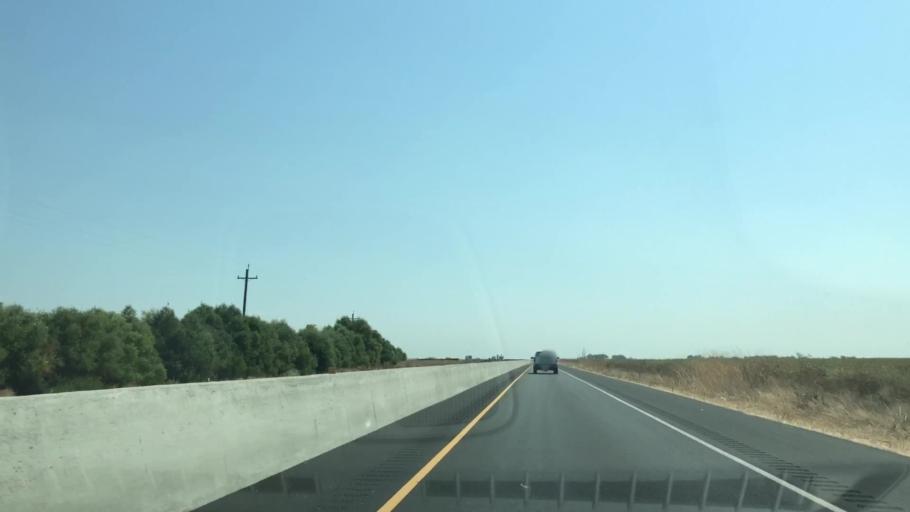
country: US
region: California
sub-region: Contra Costa County
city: Bethel Island
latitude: 38.1164
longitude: -121.5582
